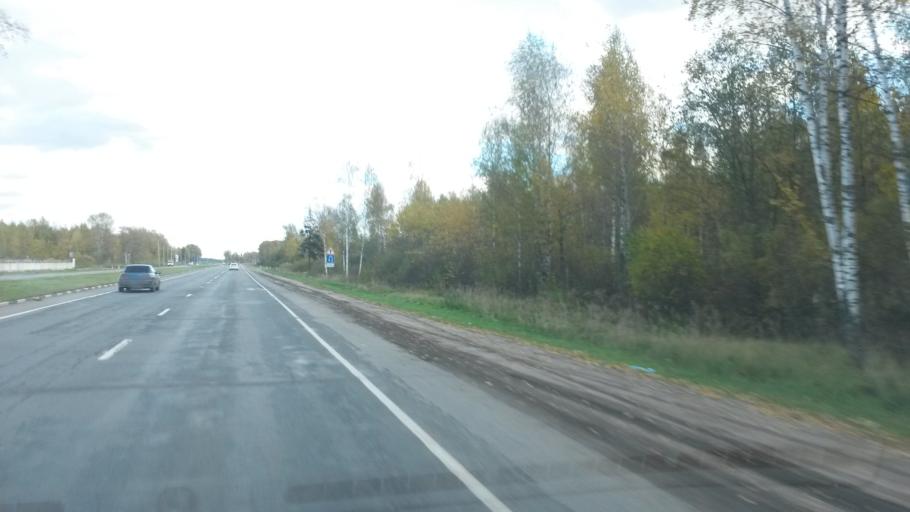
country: RU
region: Jaroslavl
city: Yaroslavl
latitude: 57.5407
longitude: 39.9830
